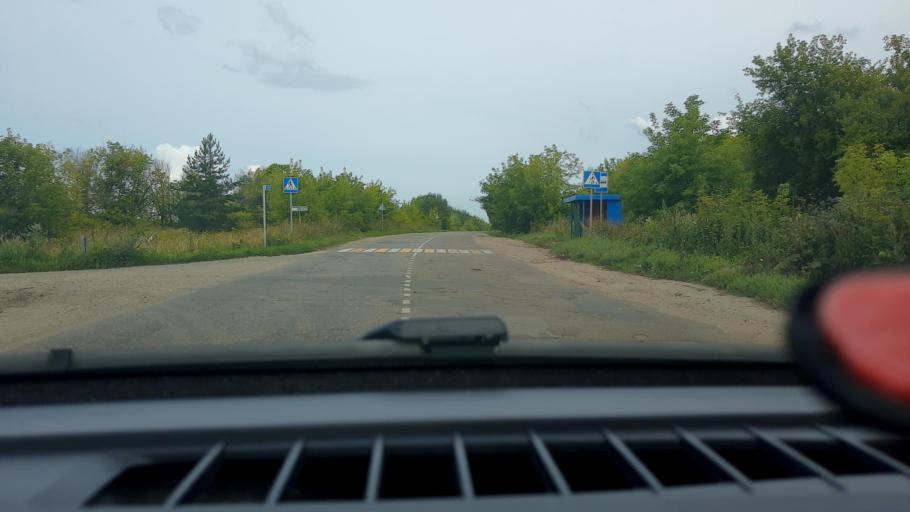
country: RU
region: Nizjnij Novgorod
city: Bogorodsk
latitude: 56.0687
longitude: 43.5810
